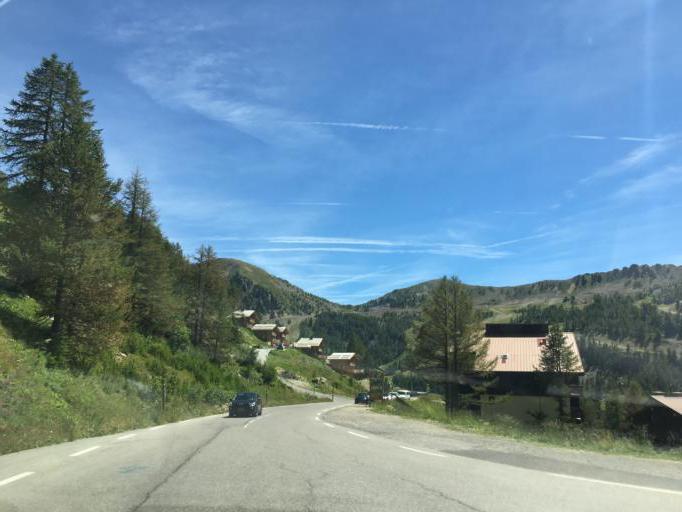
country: IT
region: Piedmont
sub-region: Provincia di Cuneo
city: Vinadio
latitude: 44.1890
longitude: 7.1599
